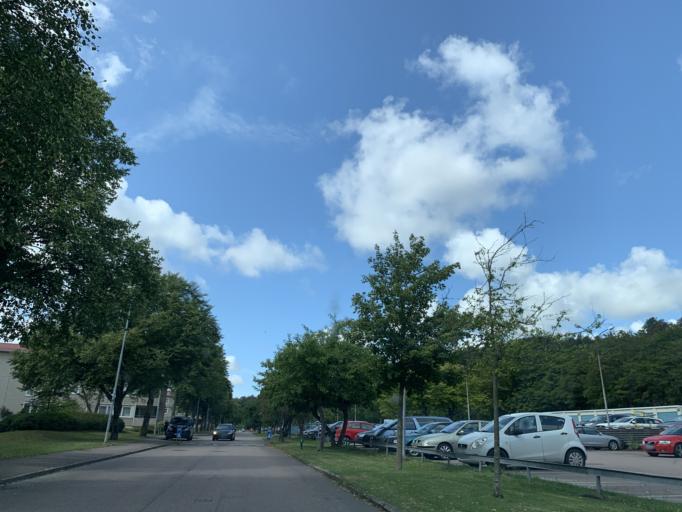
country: SE
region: Vaestra Goetaland
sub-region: Goteborg
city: Eriksbo
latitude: 57.7719
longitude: 12.0456
